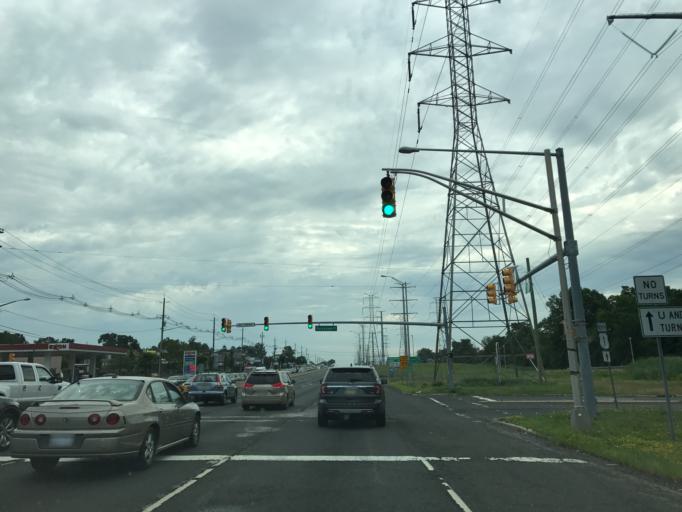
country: US
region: New Jersey
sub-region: Middlesex County
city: Fords
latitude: 40.5446
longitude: -74.3316
